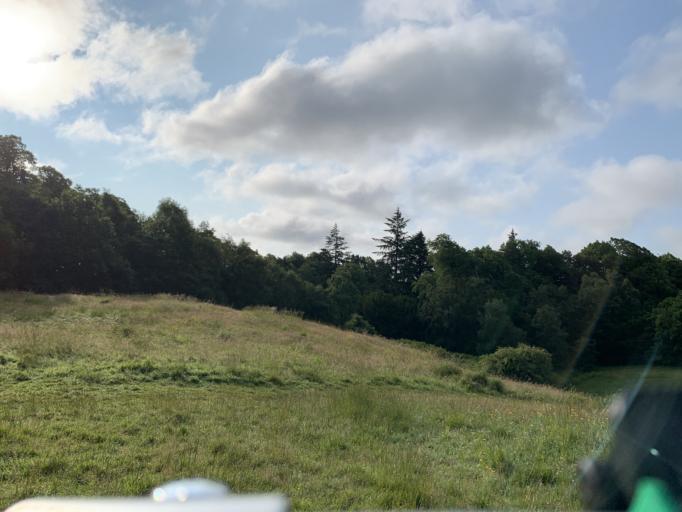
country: GB
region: Scotland
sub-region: East Renfrewshire
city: Giffnock
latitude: 55.7940
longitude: -4.3178
